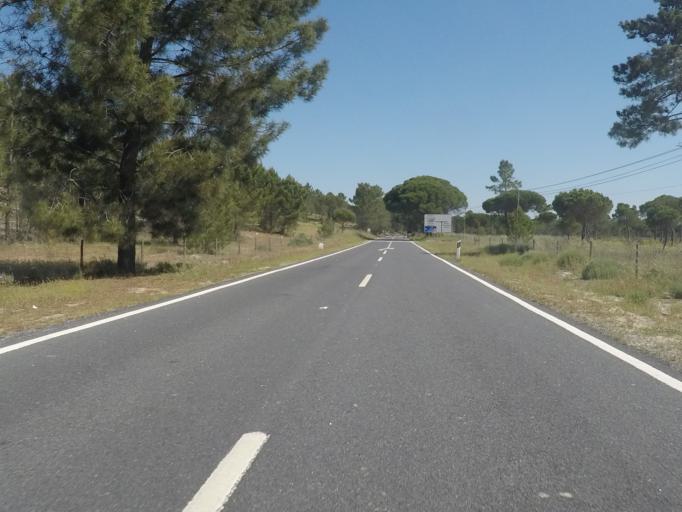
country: PT
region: Setubal
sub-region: Grandola
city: Grandola
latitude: 38.2930
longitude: -8.7266
